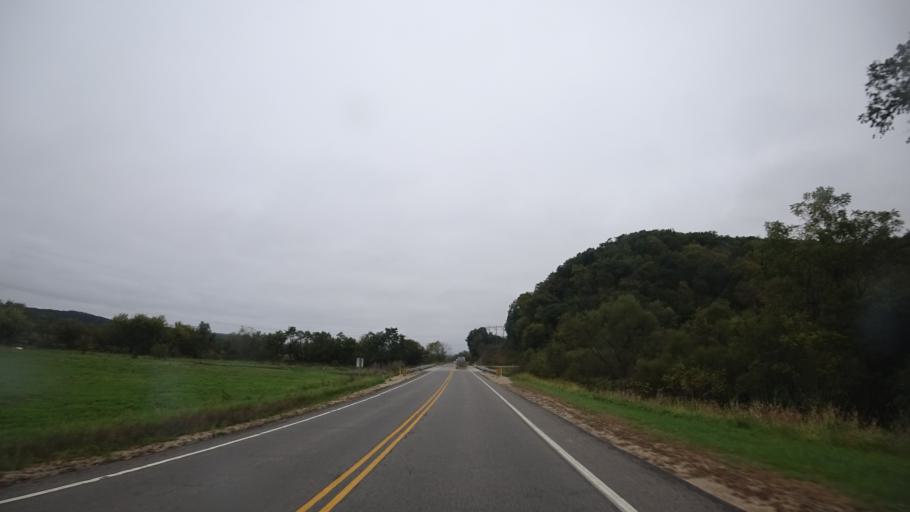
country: US
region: Wisconsin
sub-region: Crawford County
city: Prairie du Chien
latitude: 43.0789
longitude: -90.9298
